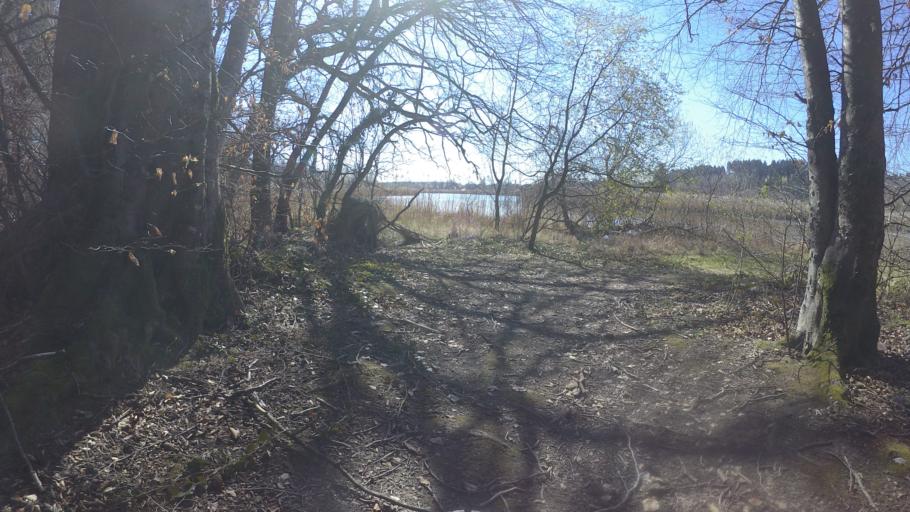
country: DE
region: Bavaria
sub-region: Upper Bavaria
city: Seeon-Seebruck
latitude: 47.9652
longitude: 12.4833
